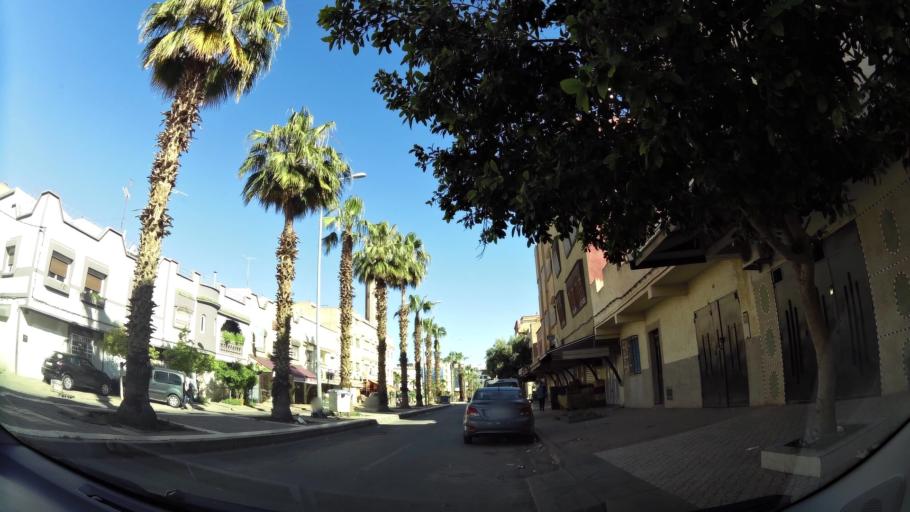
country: MA
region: Oriental
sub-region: Oujda-Angad
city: Oujda
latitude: 34.6551
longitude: -1.8968
